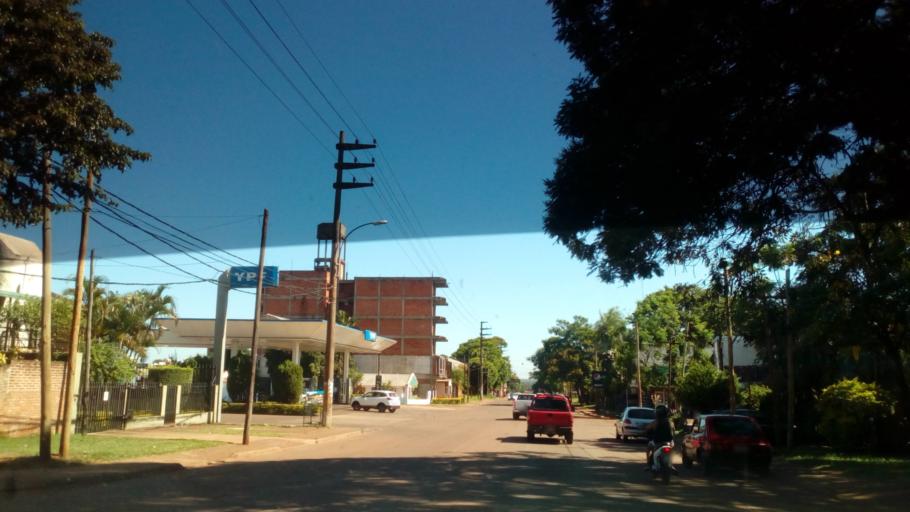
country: AR
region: Misiones
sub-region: Departamento de Capital
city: Posadas
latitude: -27.3946
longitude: -55.9128
